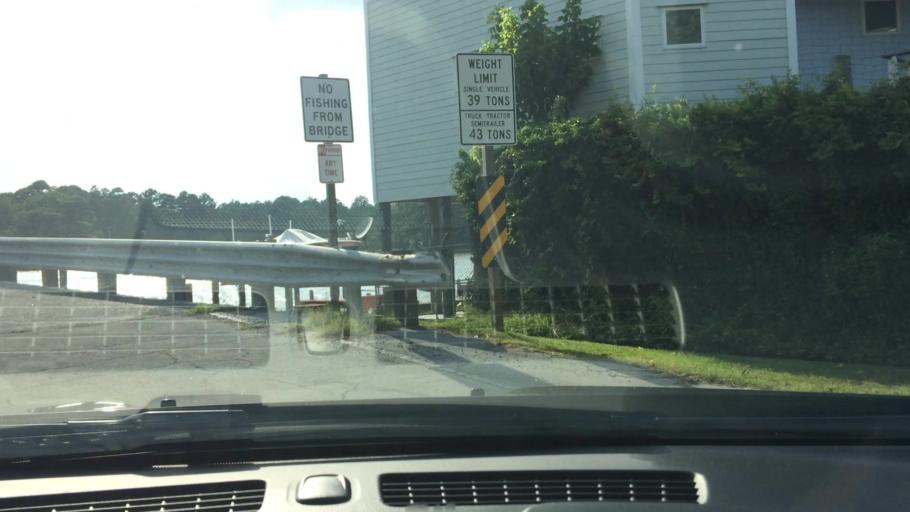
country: US
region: North Carolina
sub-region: Beaufort County
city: River Road
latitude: 35.4336
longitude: -76.9700
